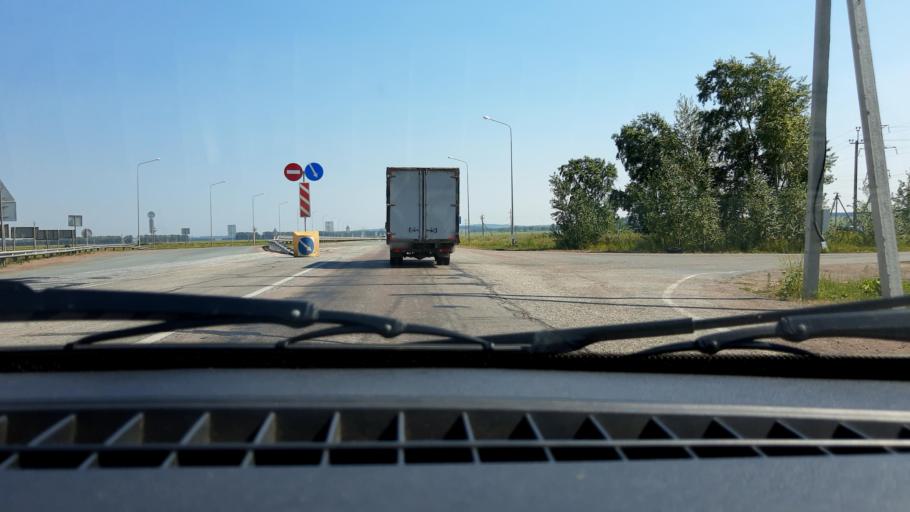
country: RU
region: Bashkortostan
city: Asanovo
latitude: 54.9000
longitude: 55.6318
